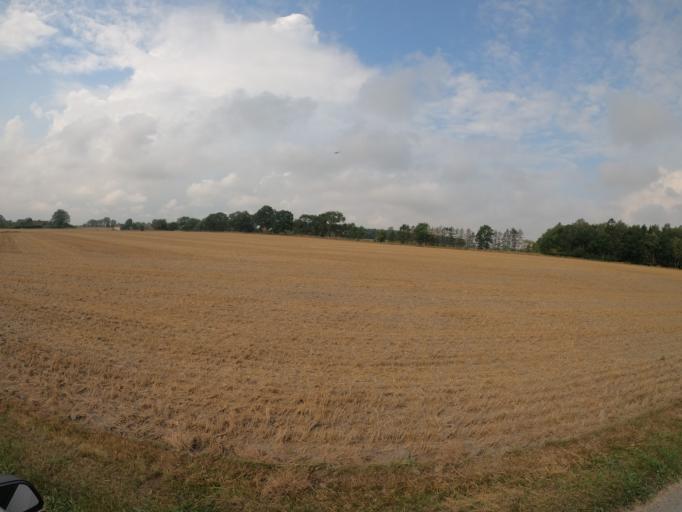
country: SE
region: Skane
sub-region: Lunds Kommun
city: Lund
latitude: 55.7236
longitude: 13.2931
